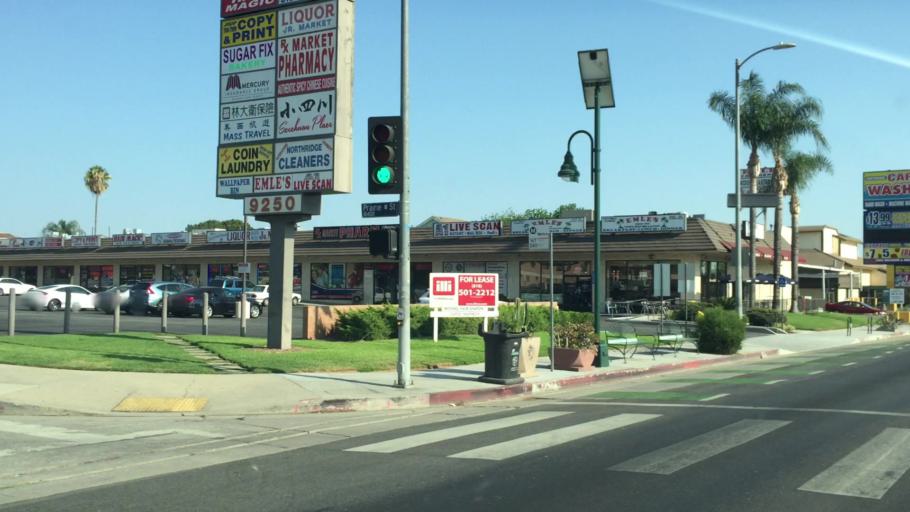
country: US
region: California
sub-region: Los Angeles County
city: Northridge
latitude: 34.2391
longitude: -118.5360
